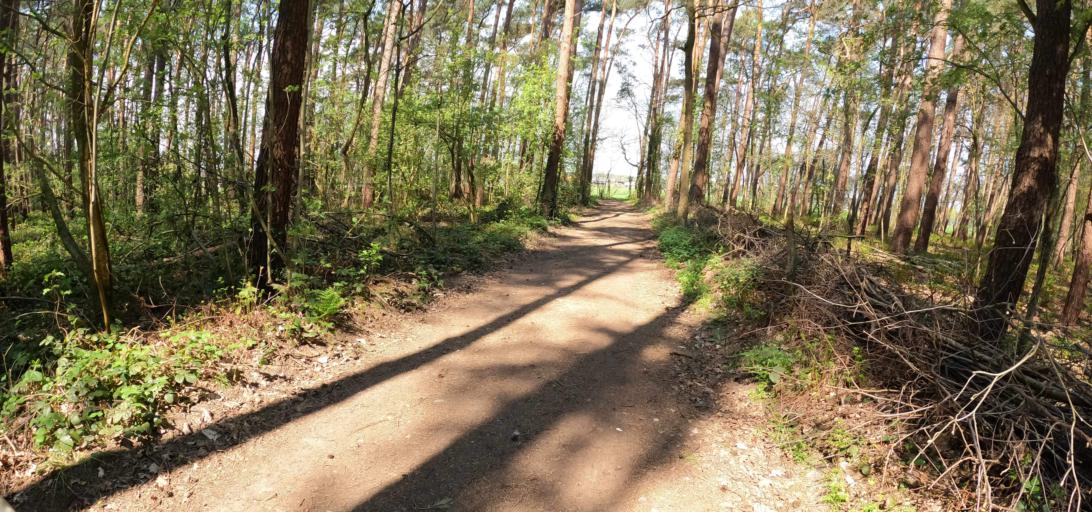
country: BE
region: Flanders
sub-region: Provincie Antwerpen
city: Vorselaar
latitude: 51.2229
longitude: 4.7684
